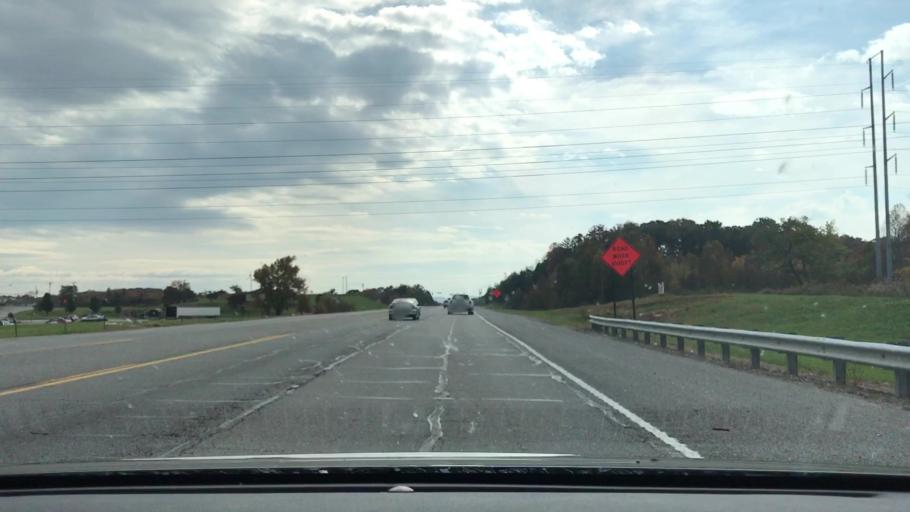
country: US
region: Tennessee
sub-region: Scott County
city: Huntsville
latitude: 36.4166
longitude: -84.5381
